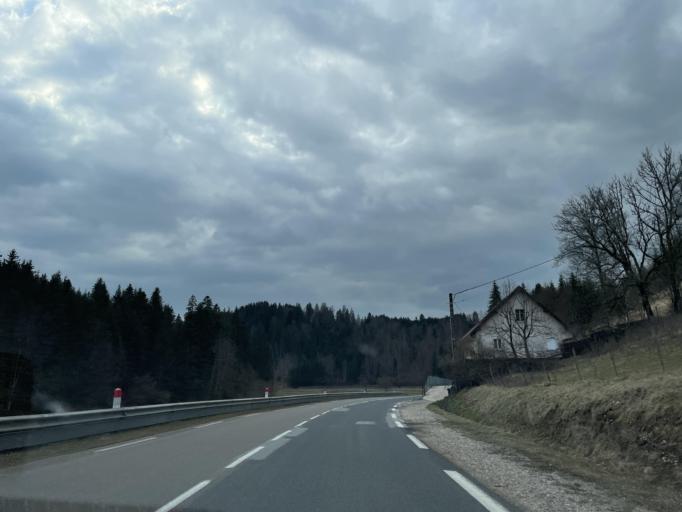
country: FR
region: Franche-Comte
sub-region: Departement du Doubs
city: Gilley
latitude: 47.0304
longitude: 6.5031
